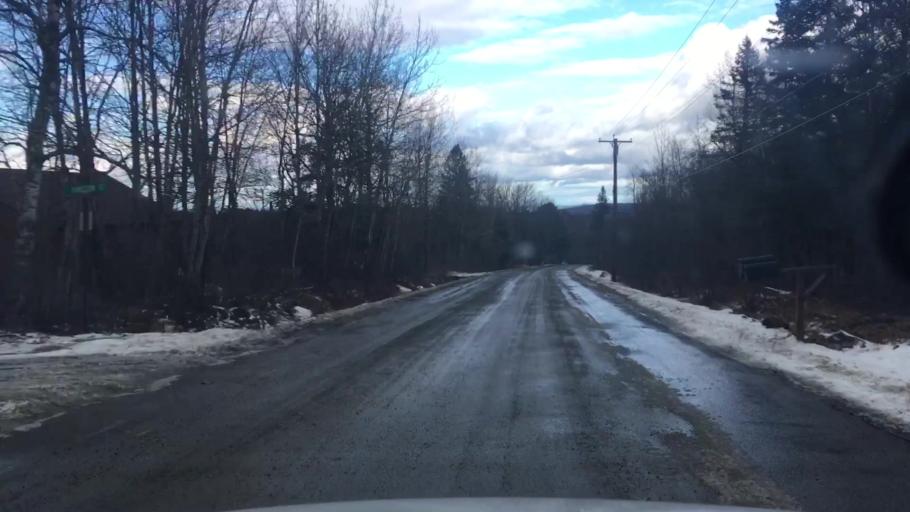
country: US
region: Maine
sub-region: Penobscot County
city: Orrington
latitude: 44.6840
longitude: -68.7539
